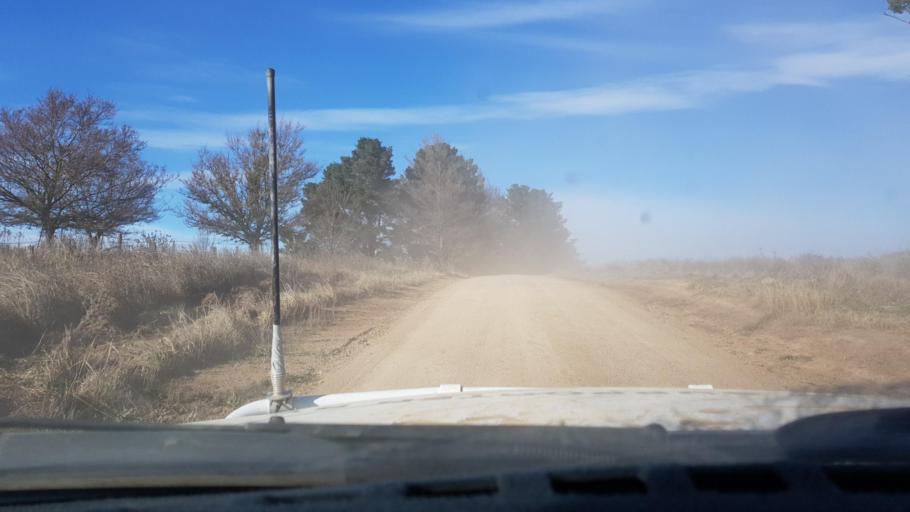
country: AU
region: New South Wales
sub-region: Armidale Dumaresq
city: Armidale
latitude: -30.6996
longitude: 151.5870
